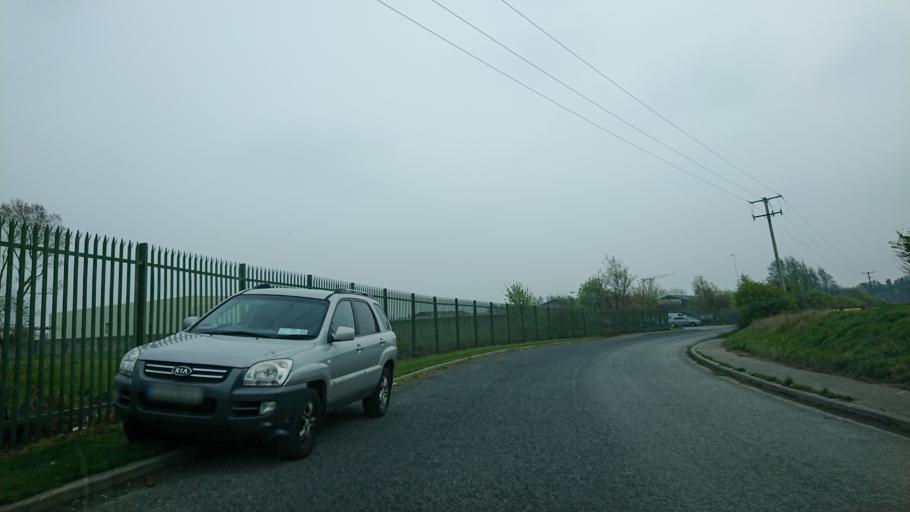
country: IE
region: Leinster
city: Ballymun
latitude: 53.4126
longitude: -6.2611
